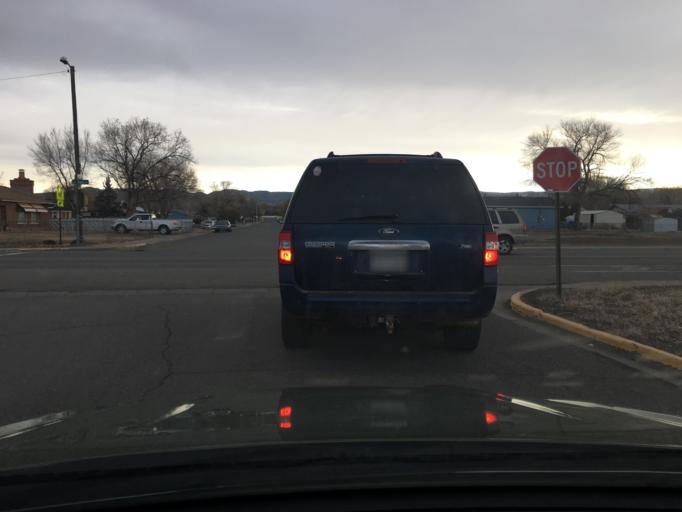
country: US
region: Colorado
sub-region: Montrose County
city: Montrose
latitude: 38.4731
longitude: -107.8662
